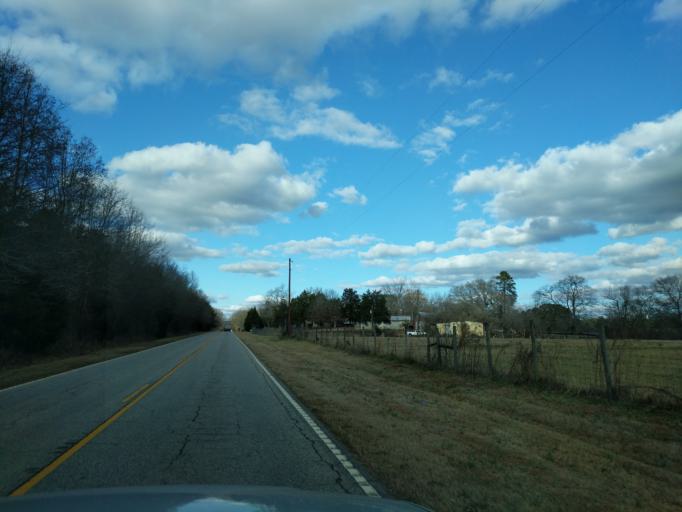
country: US
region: South Carolina
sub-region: Laurens County
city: Watts Mills
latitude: 34.6283
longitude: -81.9769
